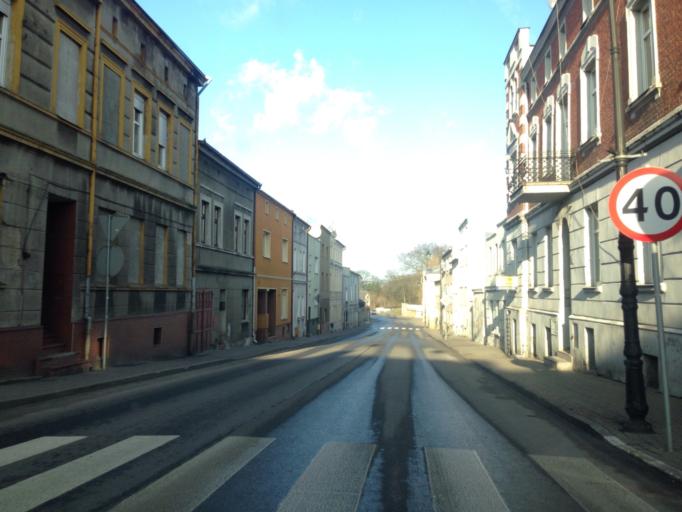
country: PL
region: Kujawsko-Pomorskie
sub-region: Powiat grudziadzki
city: Lasin
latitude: 53.5199
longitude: 19.0871
